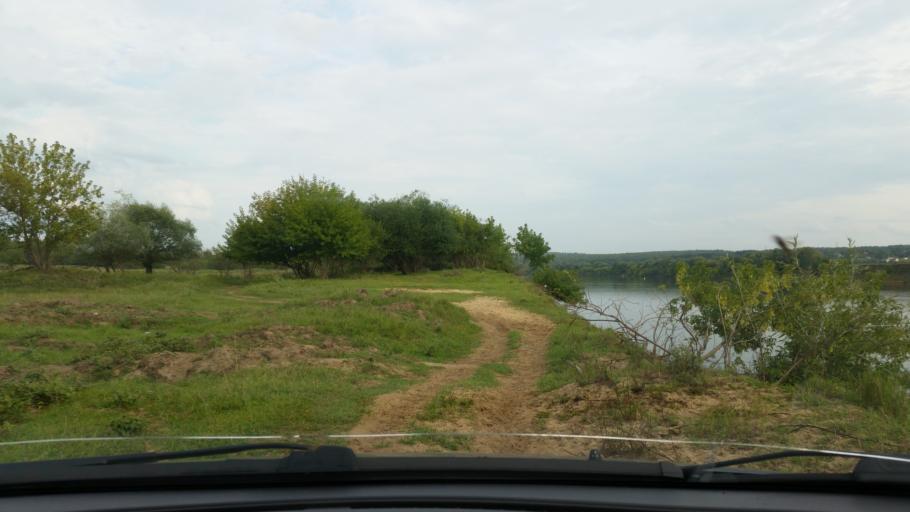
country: RU
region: Moskovskaya
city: Bol'shoye Gryzlovo
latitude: 54.8463
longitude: 37.7080
